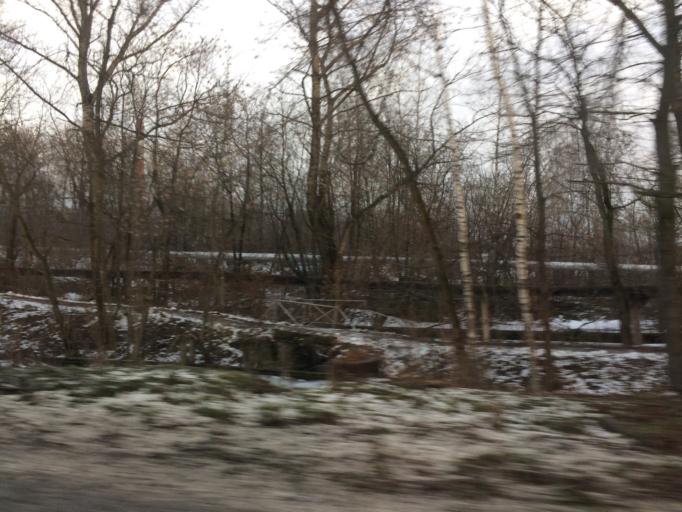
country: RU
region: Tula
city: Suvorov
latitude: 54.1309
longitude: 36.4762
